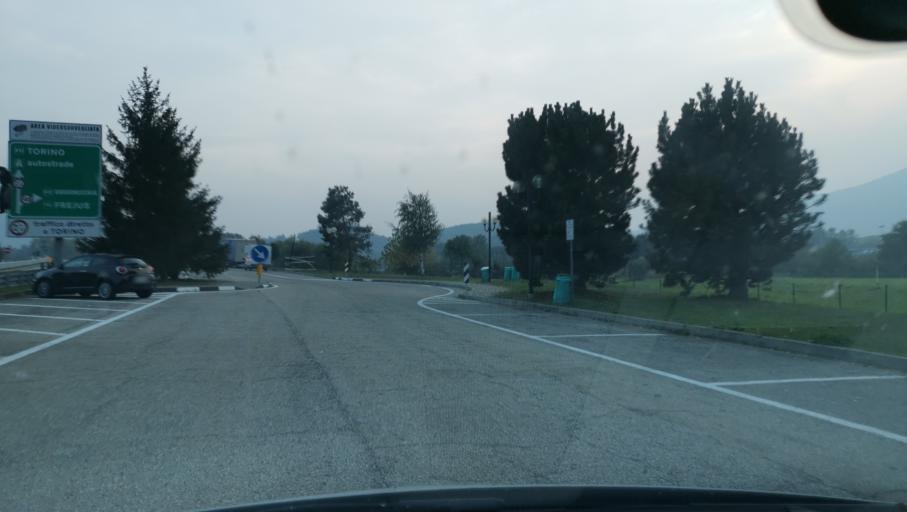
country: IT
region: Piedmont
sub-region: Provincia di Torino
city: Avigliana
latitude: 45.0970
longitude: 7.3982
